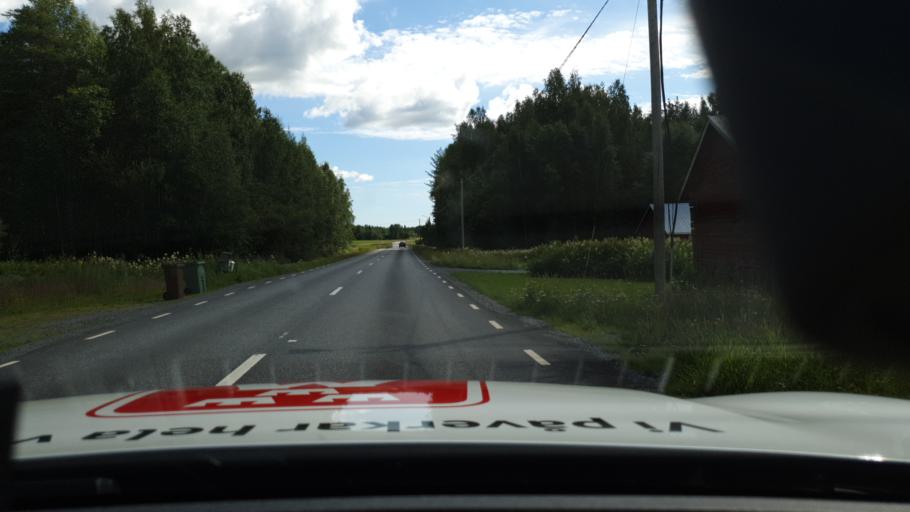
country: SE
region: Norrbotten
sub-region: Lulea Kommun
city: Gammelstad
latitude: 65.7994
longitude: 22.0566
